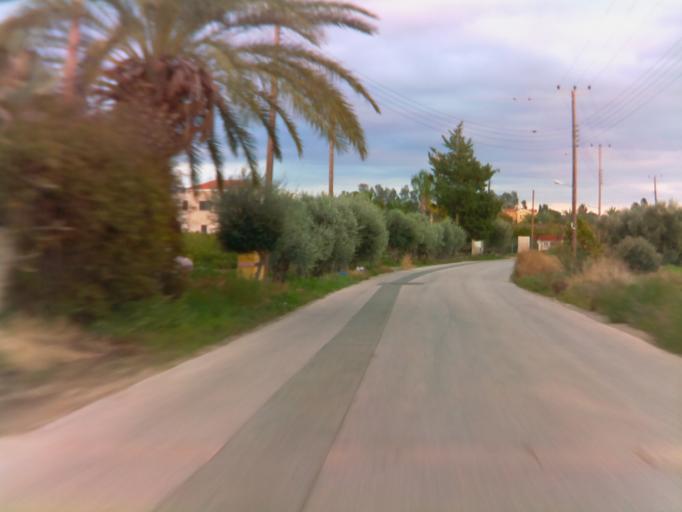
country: CY
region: Pafos
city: Pegeia
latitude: 34.8690
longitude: 32.3491
